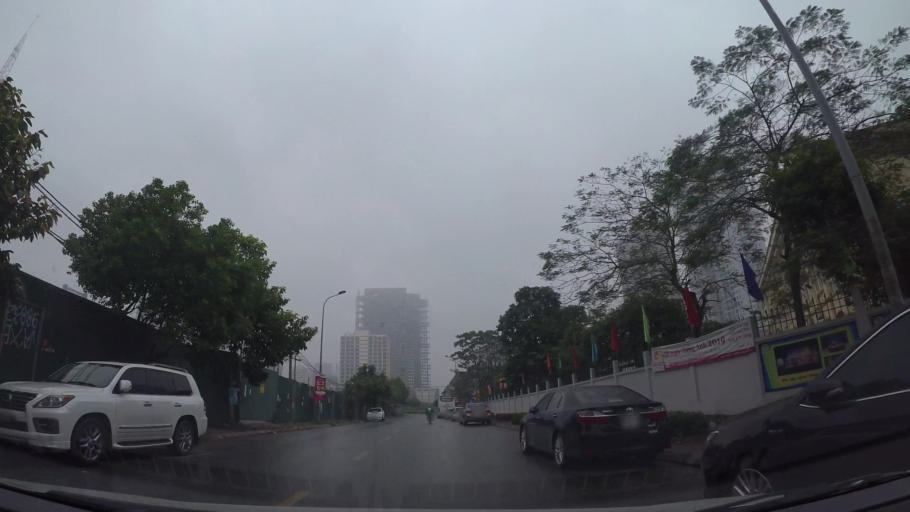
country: VN
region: Ha Noi
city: Cau Giay
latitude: 21.0184
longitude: 105.7855
